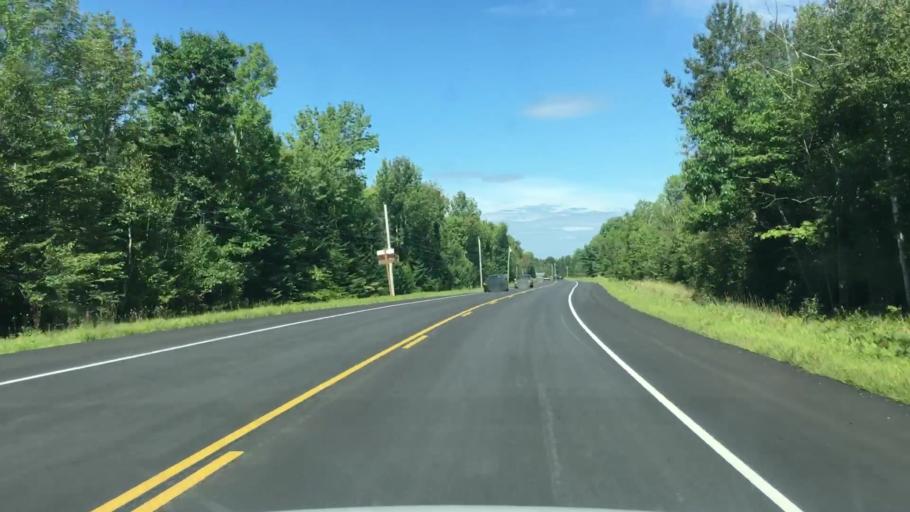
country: US
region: Maine
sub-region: Penobscot County
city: Corinna
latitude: 44.9567
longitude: -69.2635
